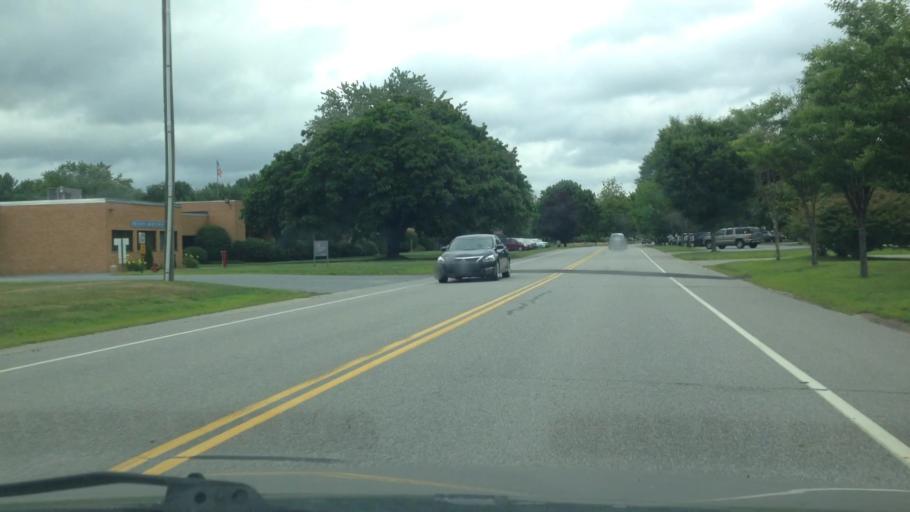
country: US
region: New Hampshire
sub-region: Cheshire County
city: Keene
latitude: 42.9201
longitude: -72.2629
